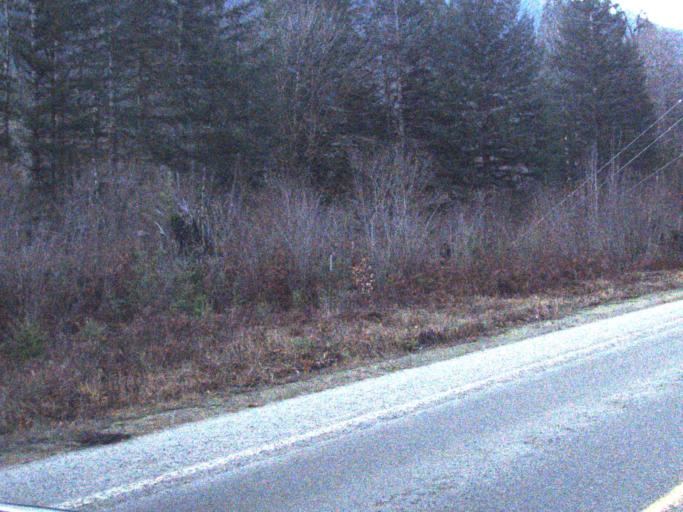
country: US
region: Washington
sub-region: Snohomish County
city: Darrington
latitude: 48.6625
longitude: -121.2862
